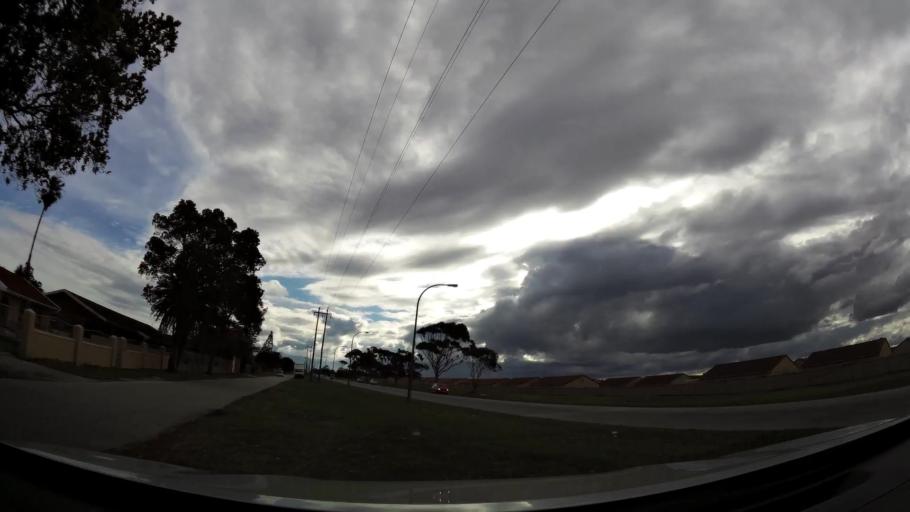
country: ZA
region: Eastern Cape
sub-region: Nelson Mandela Bay Metropolitan Municipality
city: Port Elizabeth
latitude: -33.9349
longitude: 25.4690
